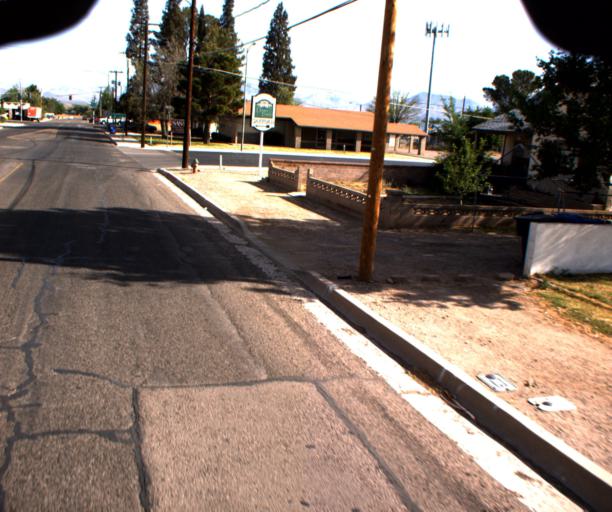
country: US
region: Arizona
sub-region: Graham County
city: Safford
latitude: 32.8329
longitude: -109.7077
